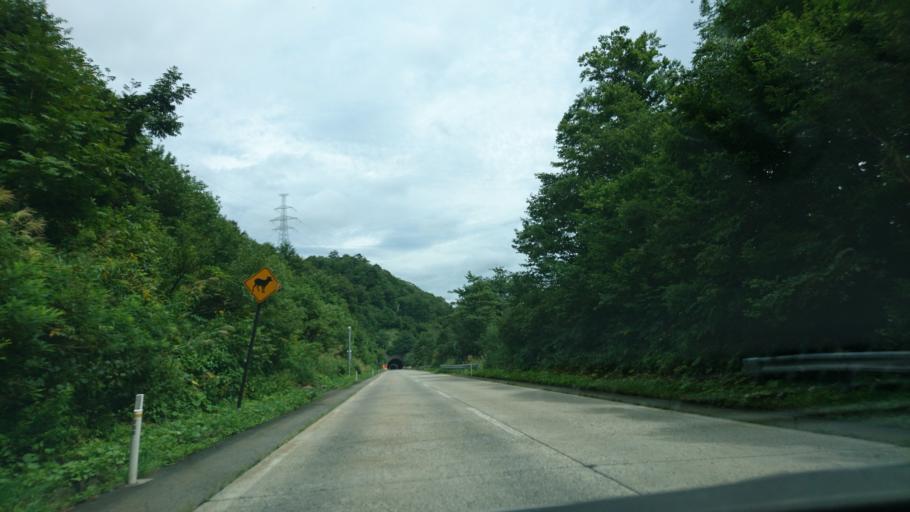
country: JP
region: Yamagata
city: Shinjo
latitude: 38.8544
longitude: 140.6043
